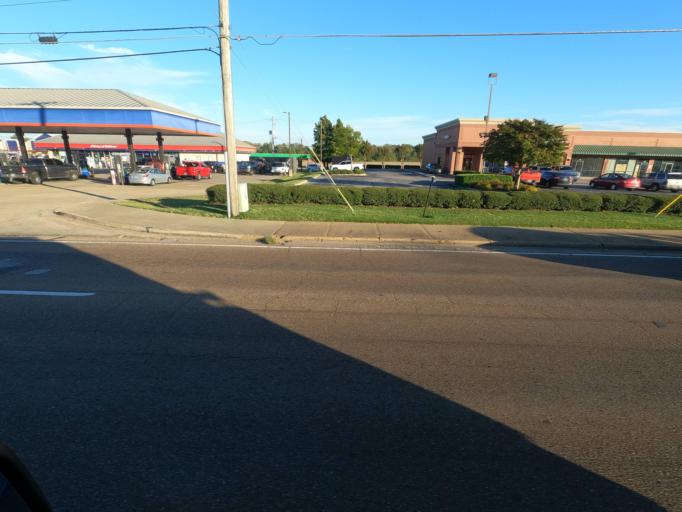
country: US
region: Tennessee
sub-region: Shelby County
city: Millington
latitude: 35.3568
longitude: -89.8949
